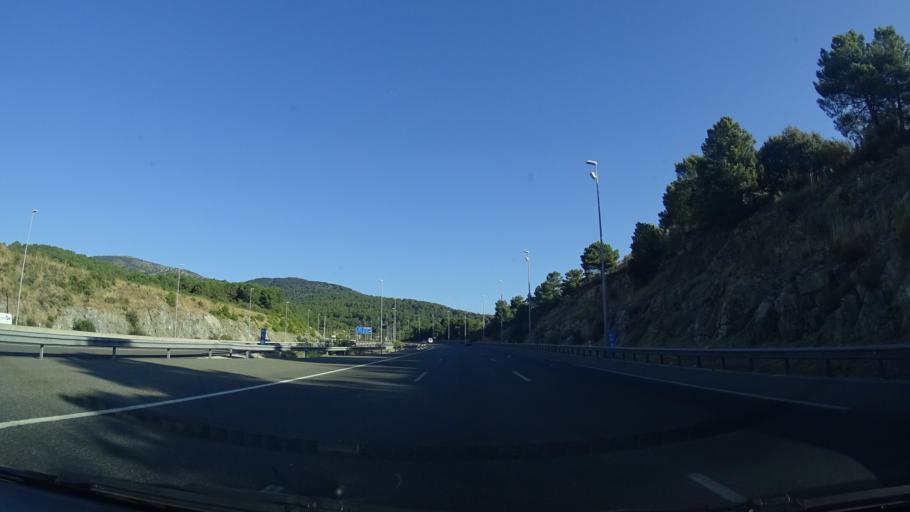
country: ES
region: Madrid
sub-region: Provincia de Madrid
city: Guadarrama
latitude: 40.6740
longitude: -4.1126
